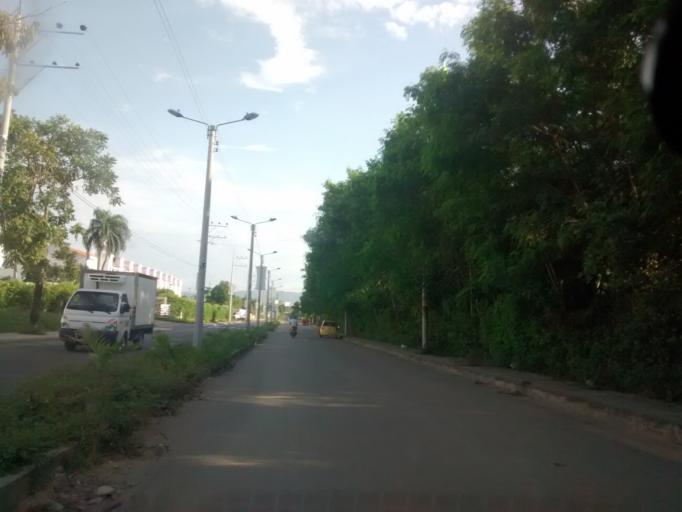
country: CO
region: Cundinamarca
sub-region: Girardot
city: Girardot City
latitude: 4.3102
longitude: -74.8156
